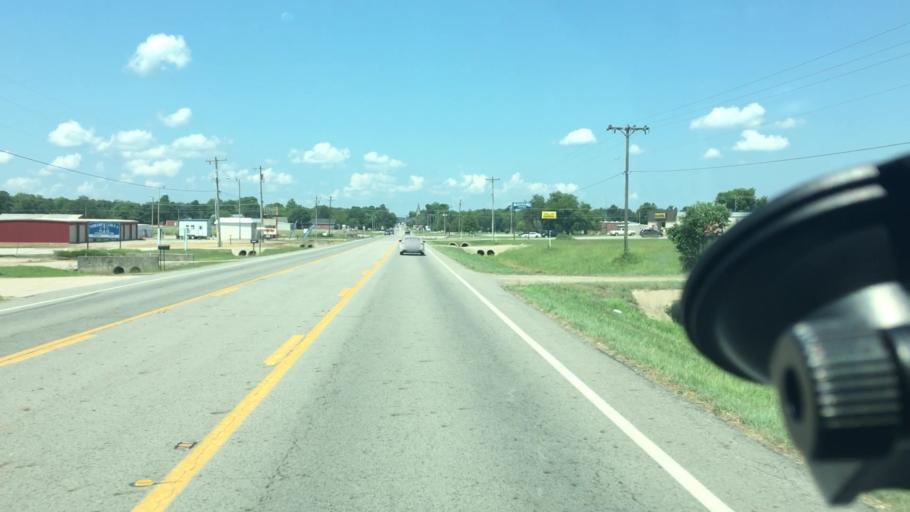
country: US
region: Arkansas
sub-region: Franklin County
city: Charleston
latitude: 35.2969
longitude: -94.0233
